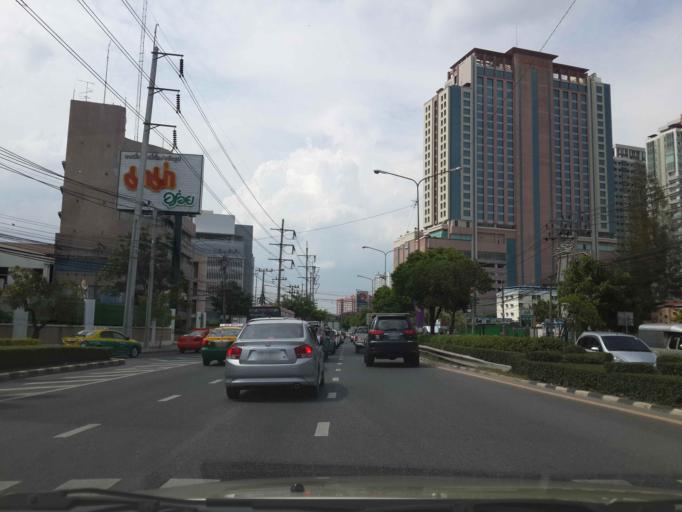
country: TH
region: Bangkok
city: Bang Kapi
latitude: 13.7520
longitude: 100.6452
